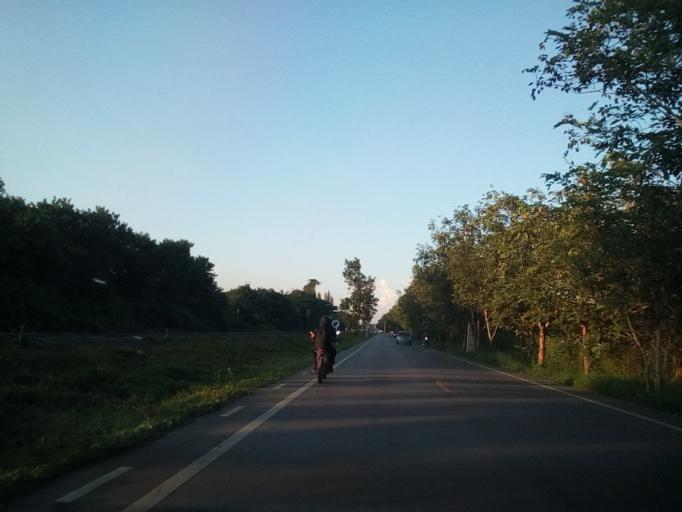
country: TH
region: Lamphun
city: Lamphun
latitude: 18.6331
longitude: 99.0411
